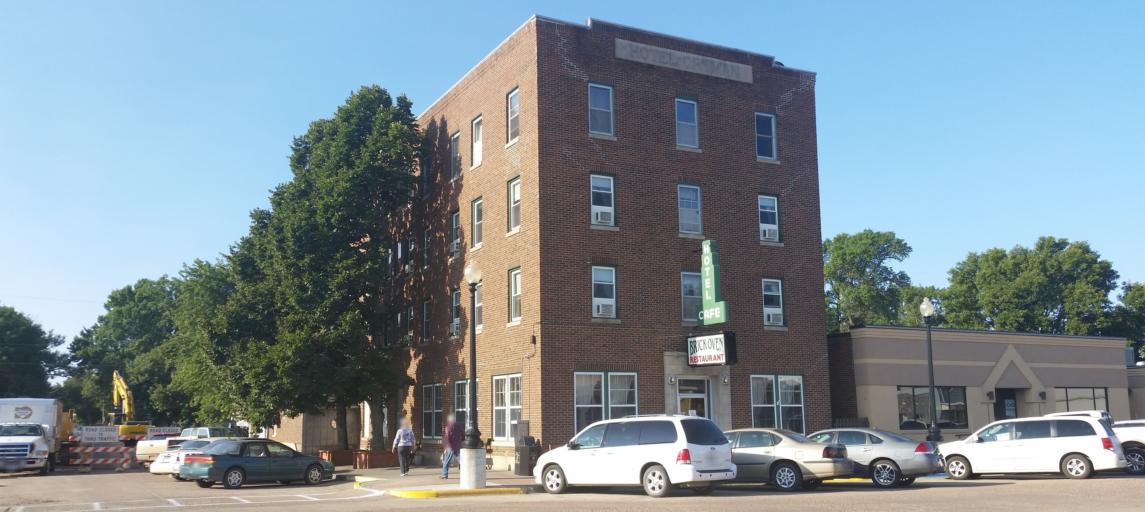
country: US
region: South Dakota
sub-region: McCook County
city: Salem
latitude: 43.5981
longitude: -97.2913
